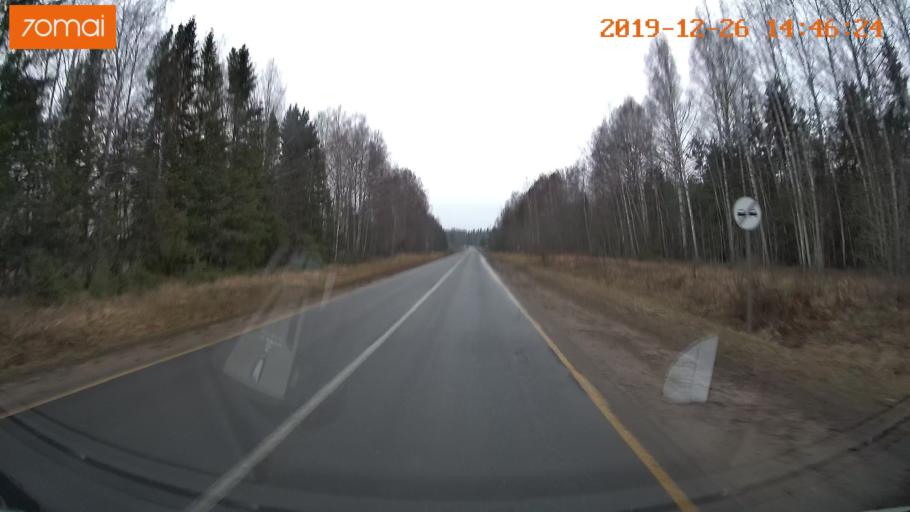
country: RU
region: Jaroslavl
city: Poshekhon'ye
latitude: 58.3357
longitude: 39.0177
